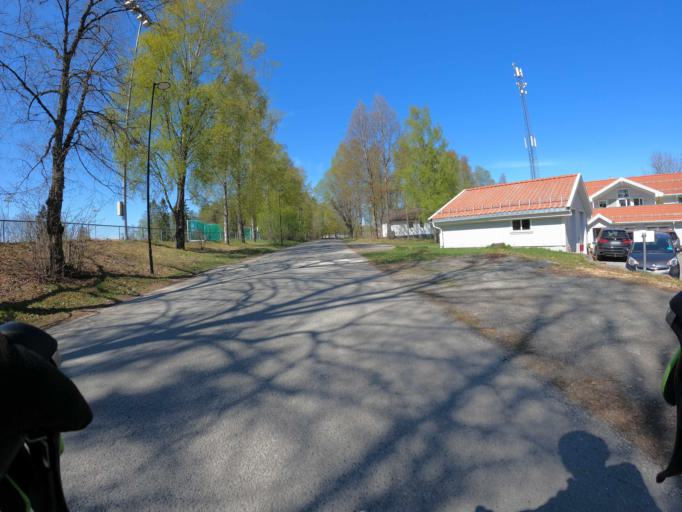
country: NO
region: Akershus
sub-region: Skedsmo
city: Lillestrom
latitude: 59.9956
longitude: 11.0445
